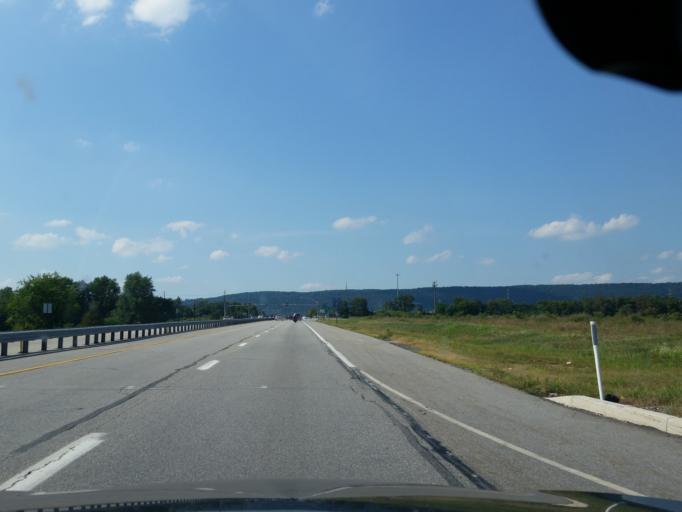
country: US
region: Pennsylvania
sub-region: Cumberland County
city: Mechanicsburg
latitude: 40.2650
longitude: -77.0425
